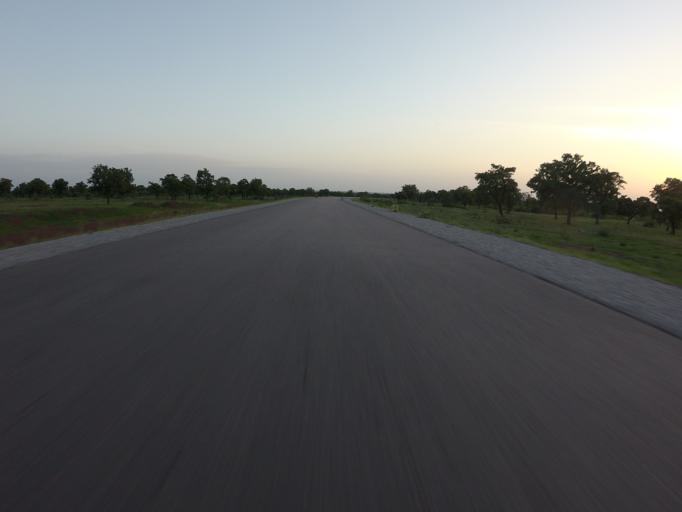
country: GH
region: Northern
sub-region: Yendi
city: Yendi
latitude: 9.9403
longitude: -0.1683
